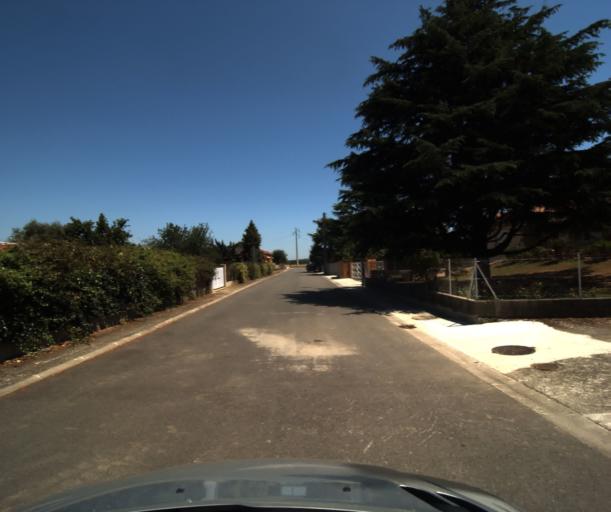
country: FR
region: Midi-Pyrenees
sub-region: Departement de la Haute-Garonne
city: Roquettes
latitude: 43.4961
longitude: 1.3795
